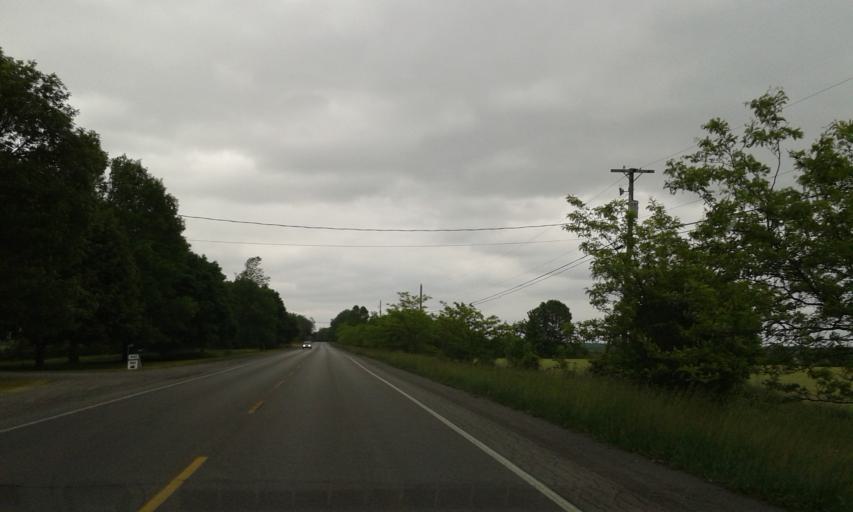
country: CA
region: Ontario
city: Prince Edward
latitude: 43.9726
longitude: -77.2735
